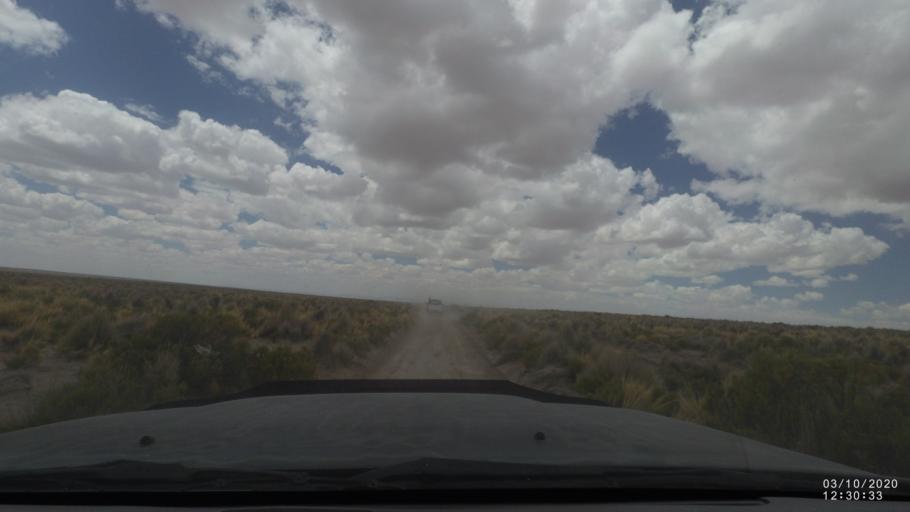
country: BO
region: Oruro
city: Poopo
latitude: -18.6867
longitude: -67.5432
